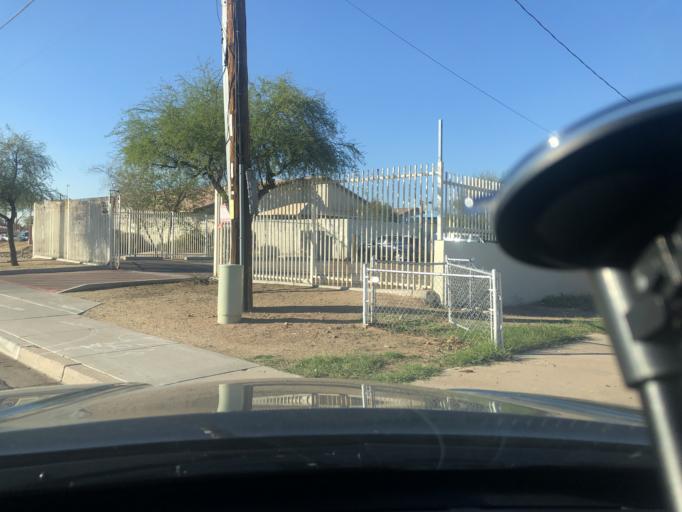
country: US
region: Arizona
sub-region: Maricopa County
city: Phoenix
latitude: 33.4551
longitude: -112.0327
